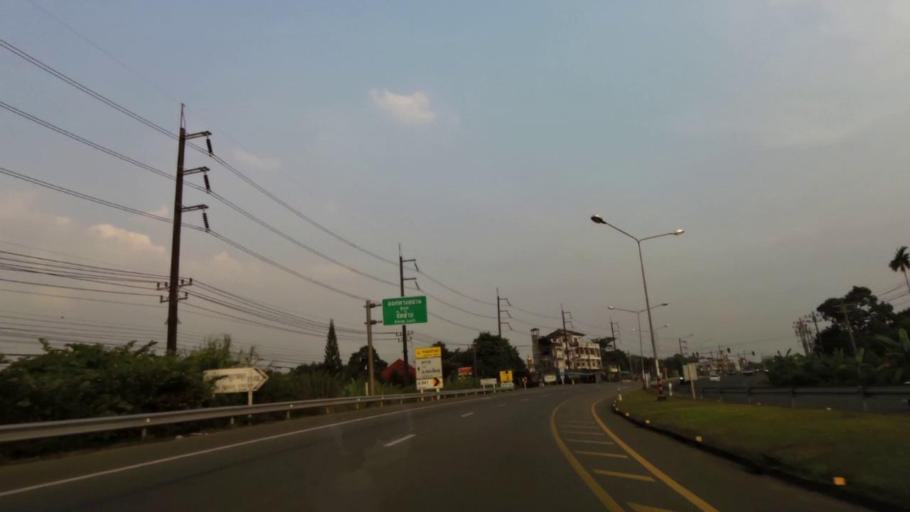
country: TH
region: Chanthaburi
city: Khlung
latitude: 12.4658
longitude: 102.2208
